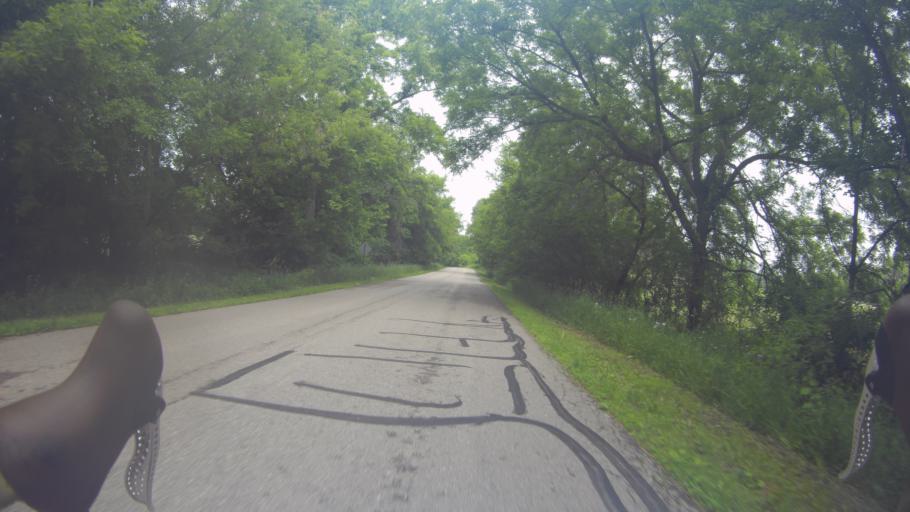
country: US
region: Wisconsin
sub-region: Jefferson County
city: Cambridge
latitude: 42.9613
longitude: -89.0052
